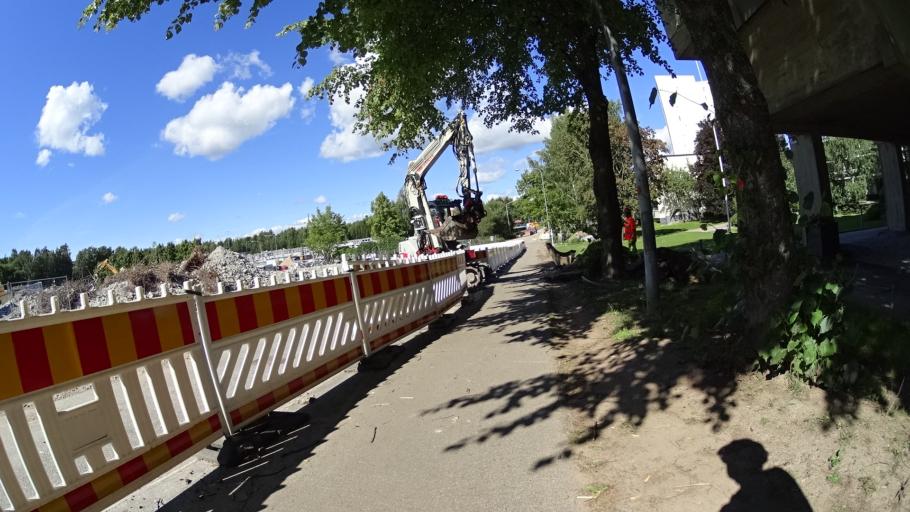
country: FI
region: Uusimaa
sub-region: Helsinki
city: Koukkuniemi
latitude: 60.1693
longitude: 24.7612
